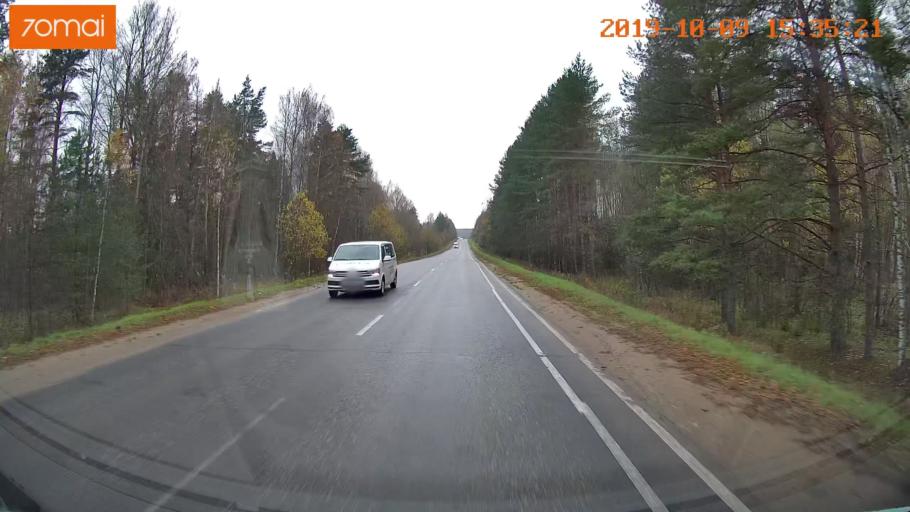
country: RU
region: Kostroma
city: Oktyabr'skiy
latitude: 57.9329
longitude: 41.2288
